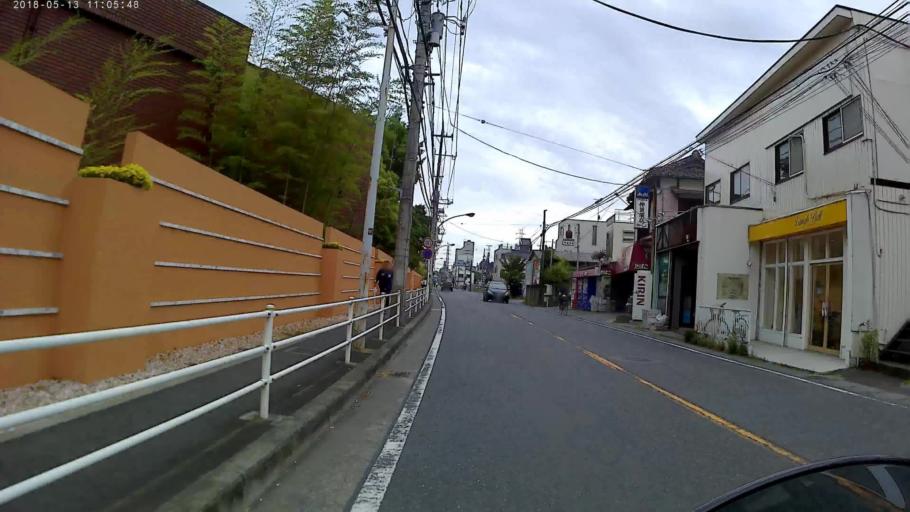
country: JP
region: Tokyo
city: Chofugaoka
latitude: 35.5940
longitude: 139.6143
